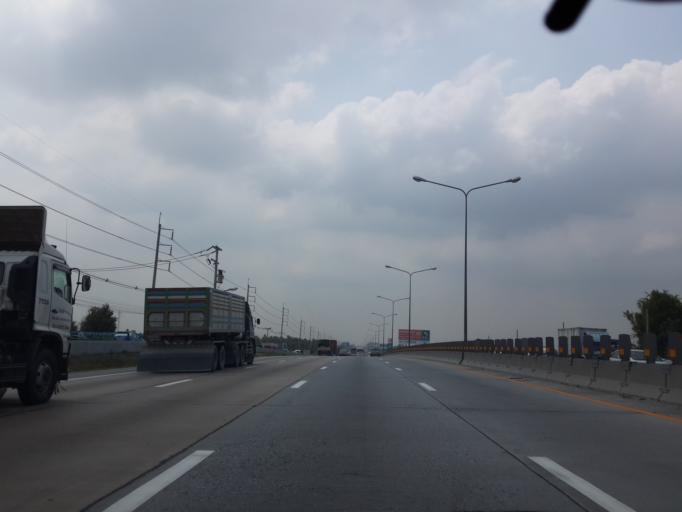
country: TH
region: Chon Buri
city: Si Racha
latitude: 13.2028
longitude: 101.0026
